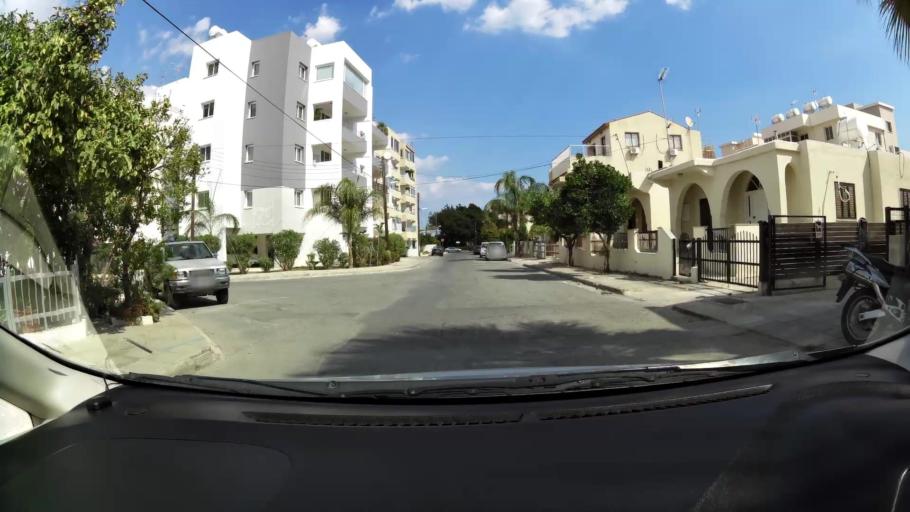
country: CY
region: Larnaka
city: Larnaca
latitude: 34.9188
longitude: 33.6108
